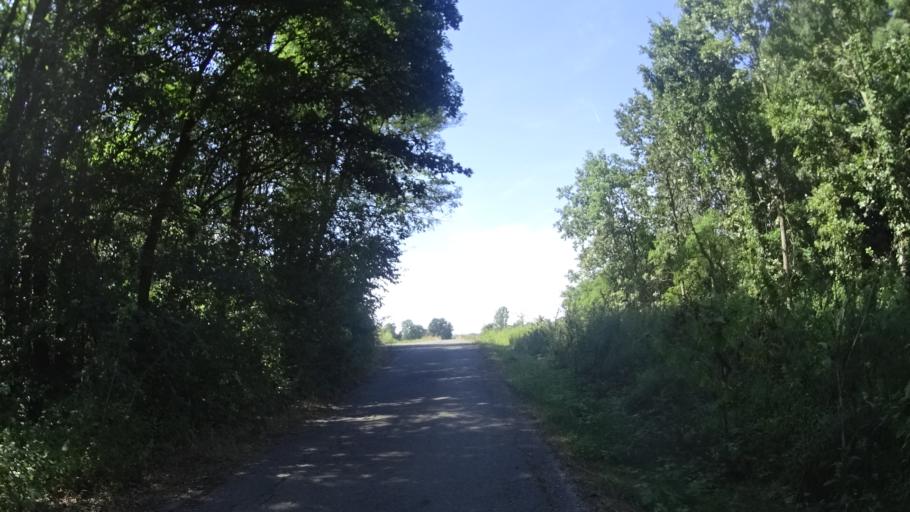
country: AT
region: Lower Austria
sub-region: Politischer Bezirk Ganserndorf
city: Angern an der March
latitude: 48.3710
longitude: 16.8555
